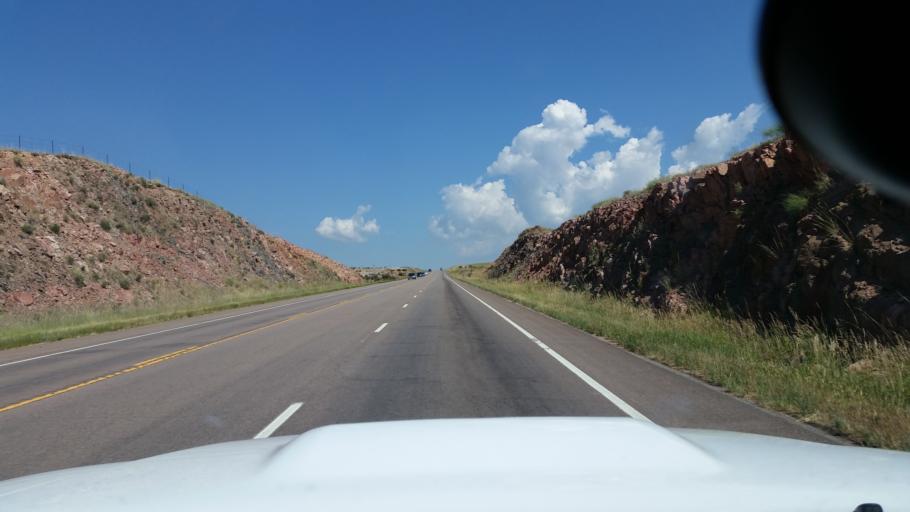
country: US
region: Colorado
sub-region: Larimer County
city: Laporte
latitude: 40.8427
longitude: -105.2517
